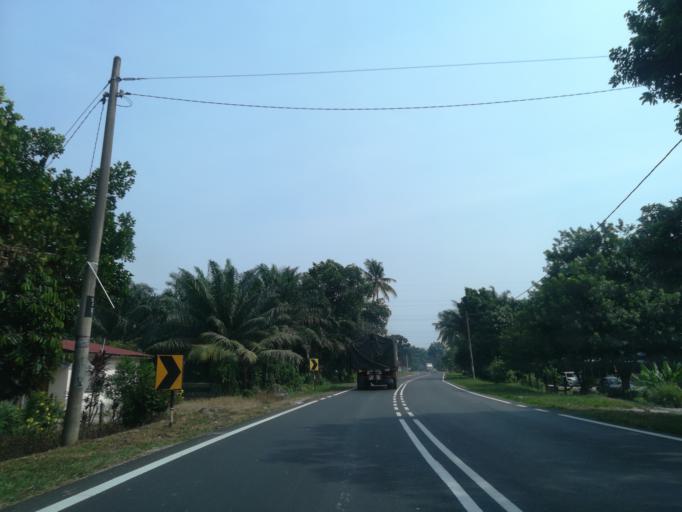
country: MY
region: Penang
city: Tasek Glugor
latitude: 5.4521
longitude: 100.5473
